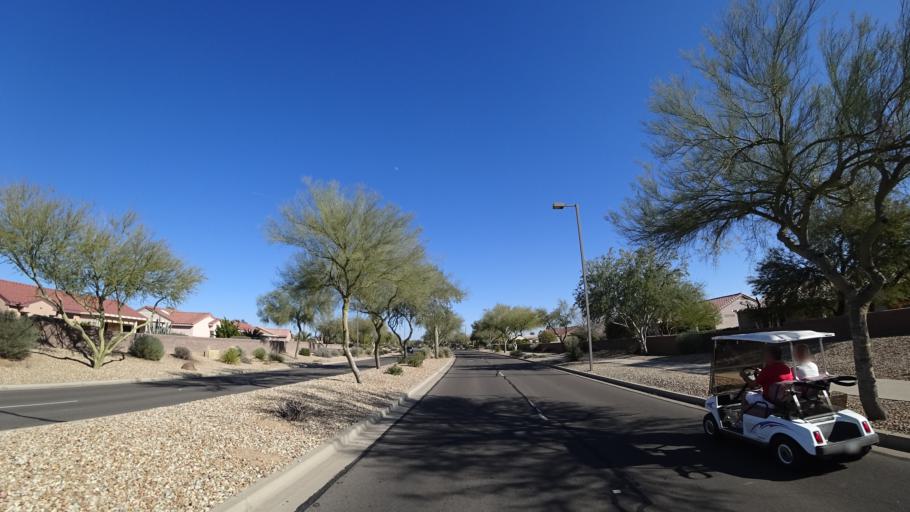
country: US
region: Arizona
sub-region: Maricopa County
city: Sun City West
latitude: 33.6690
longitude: -112.4056
